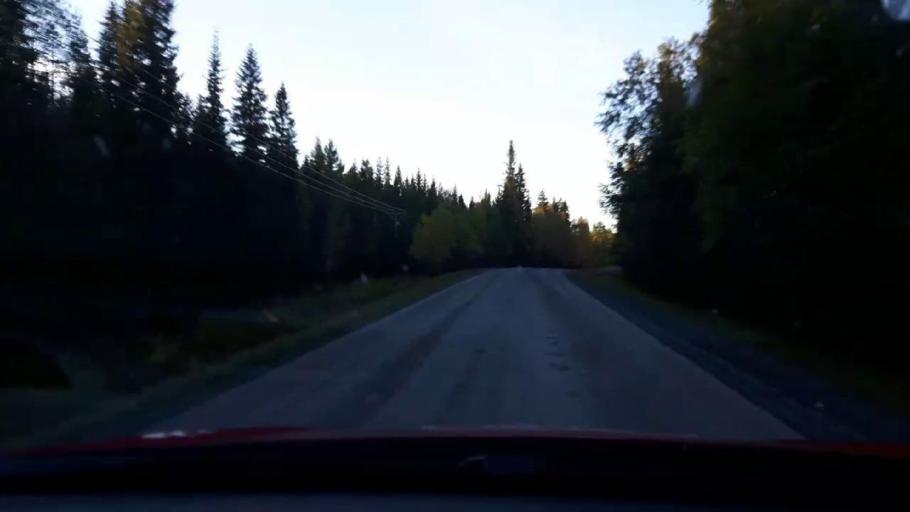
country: SE
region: Jaemtland
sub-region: Krokoms Kommun
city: Krokom
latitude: 63.4343
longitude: 14.4248
